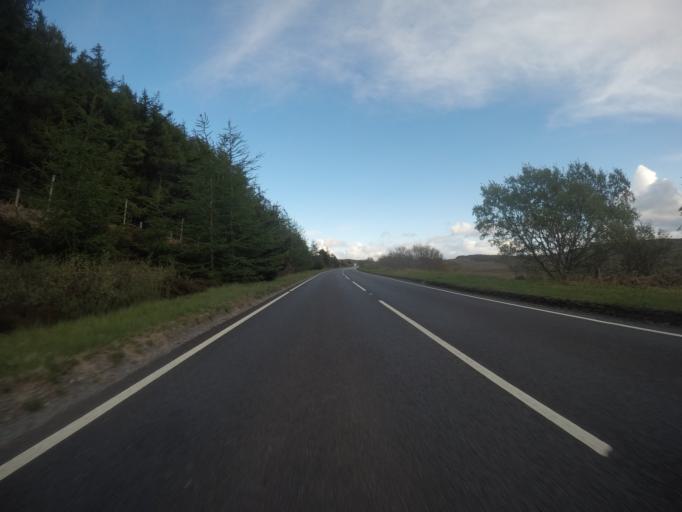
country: GB
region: Scotland
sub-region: Highland
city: Portree
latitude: 57.5263
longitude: -6.3463
